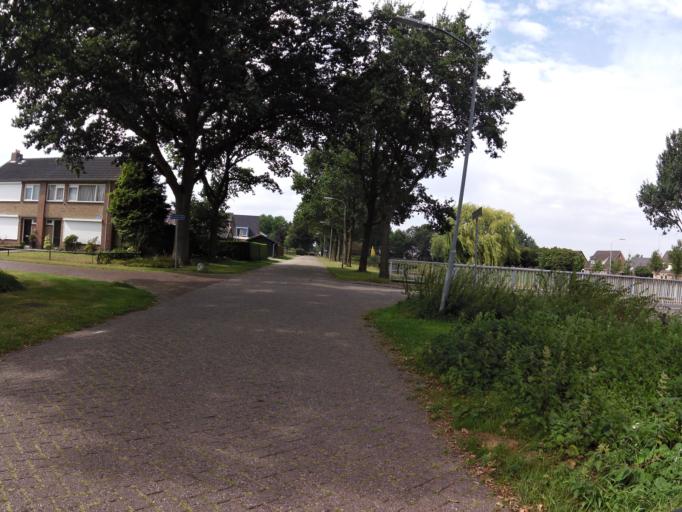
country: NL
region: Drenthe
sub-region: Gemeente Emmen
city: Klazienaveen
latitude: 52.6732
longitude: 6.9777
